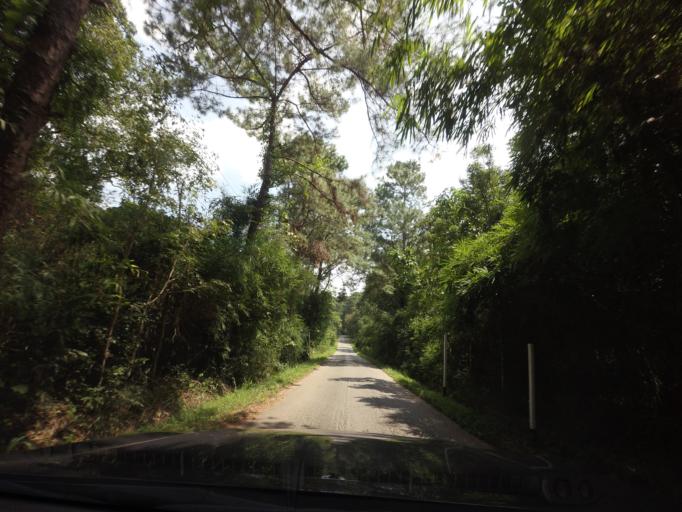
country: TH
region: Loei
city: Phu Ruea
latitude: 17.4741
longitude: 101.3528
